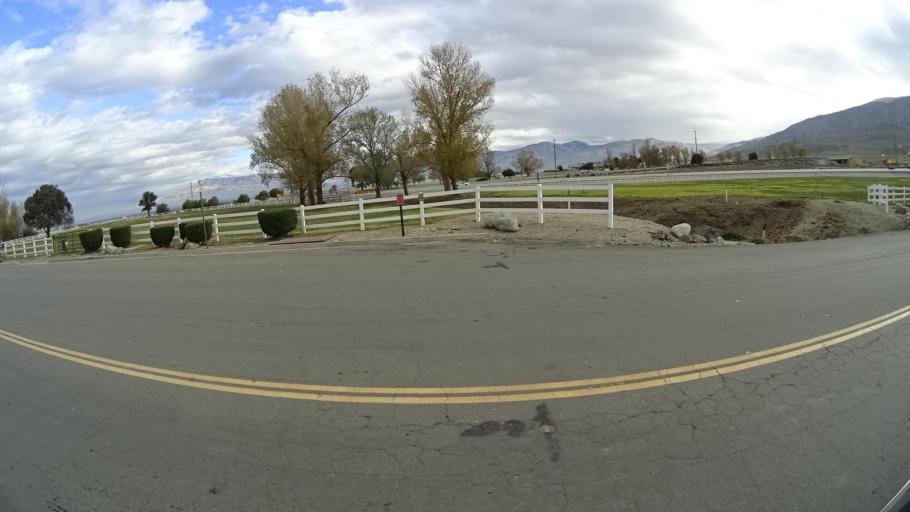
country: US
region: California
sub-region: Kern County
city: Frazier Park
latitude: 34.9410
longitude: -118.9327
